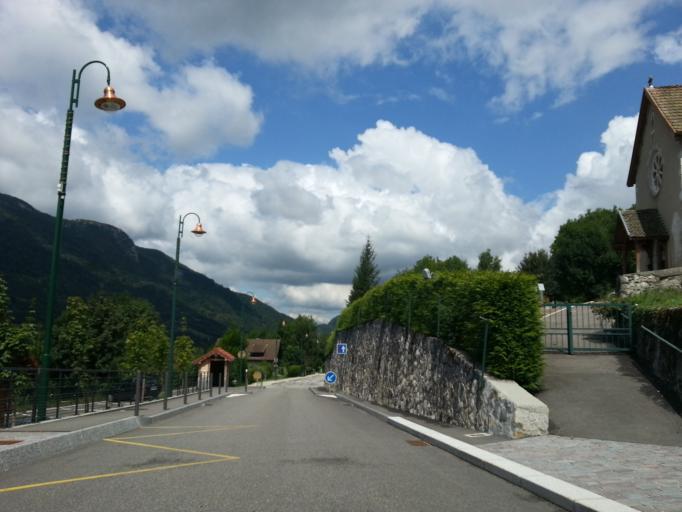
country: FR
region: Rhone-Alpes
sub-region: Departement de la Haute-Savoie
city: Menthon-Saint-Bernard
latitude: 45.8686
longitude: 6.2184
